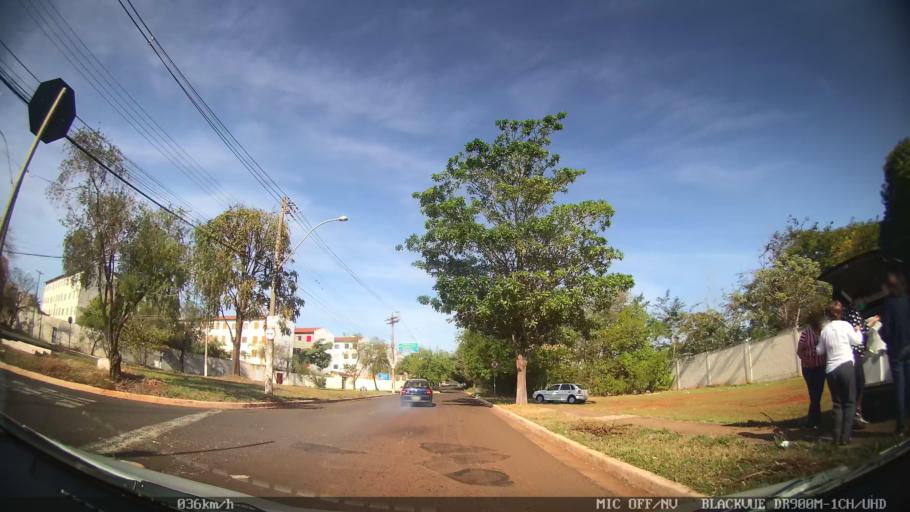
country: BR
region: Sao Paulo
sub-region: Ribeirao Preto
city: Ribeirao Preto
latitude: -21.2128
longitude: -47.8275
